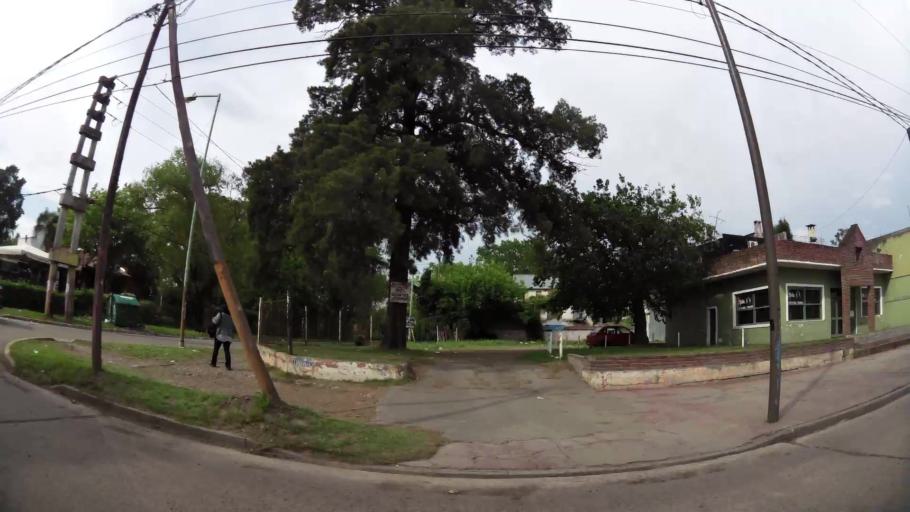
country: AR
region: Buenos Aires
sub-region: Partido de Quilmes
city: Quilmes
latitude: -34.7081
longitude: -58.2272
